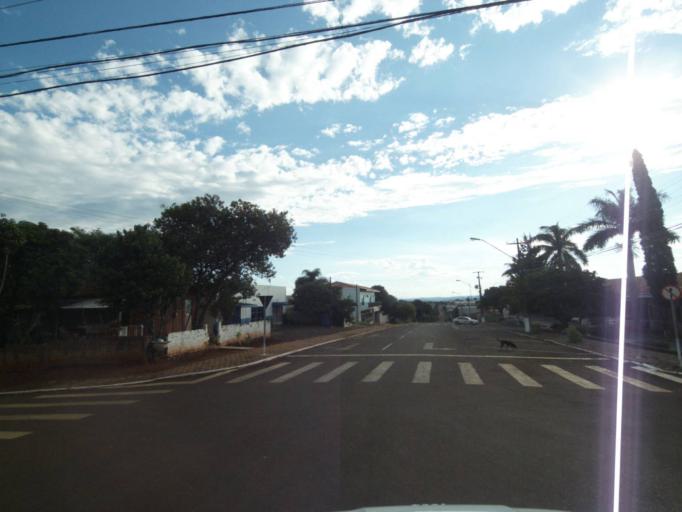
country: BR
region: Parana
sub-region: Laranjeiras Do Sul
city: Laranjeiras do Sul
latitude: -25.4906
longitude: -52.5251
